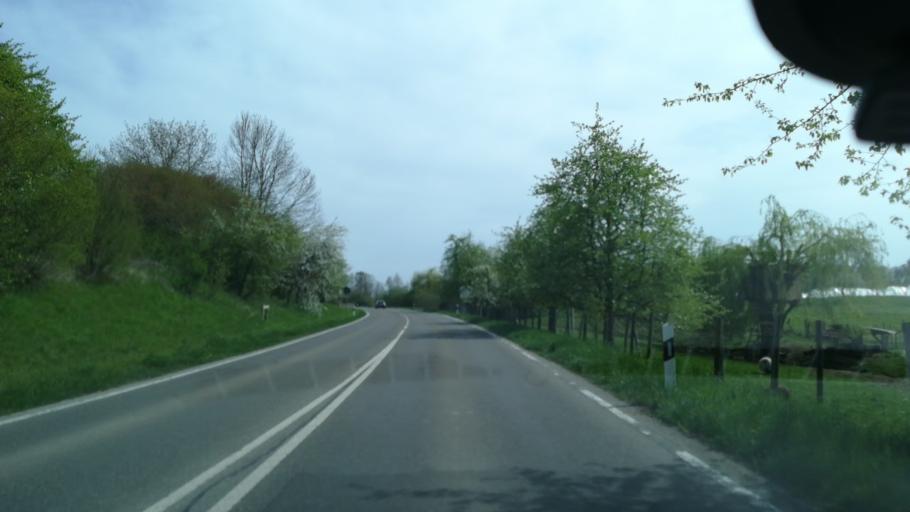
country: DE
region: Baden-Wuerttemberg
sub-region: Tuebingen Region
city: Uberlingen
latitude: 47.7266
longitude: 9.1585
